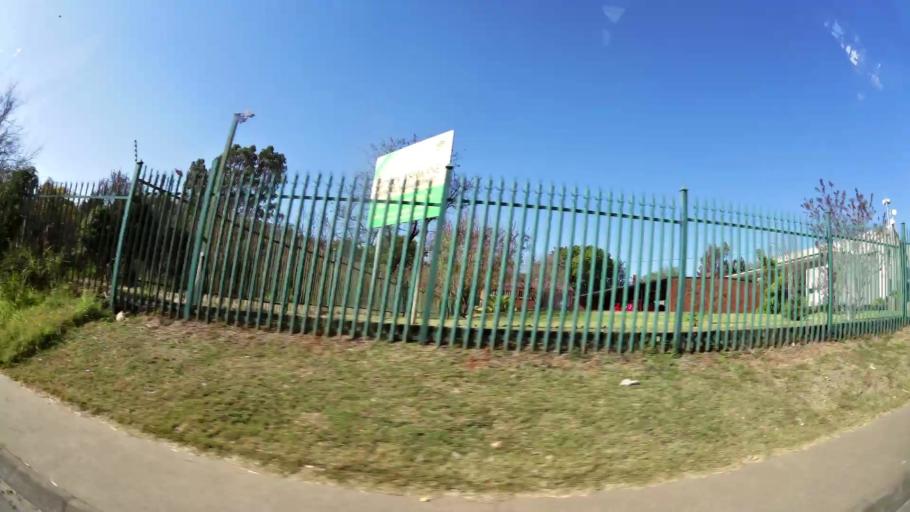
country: ZA
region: Gauteng
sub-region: City of Tshwane Metropolitan Municipality
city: Pretoria
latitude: -25.7309
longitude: 28.2047
